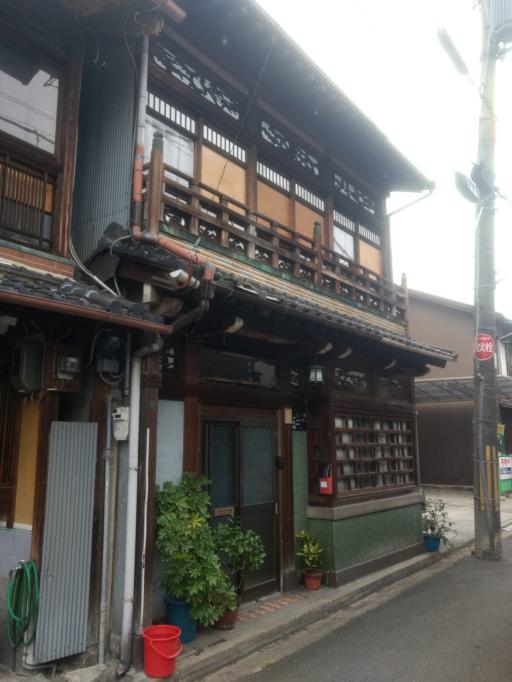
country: JP
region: Kyoto
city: Yawata
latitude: 34.8820
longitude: 135.6830
